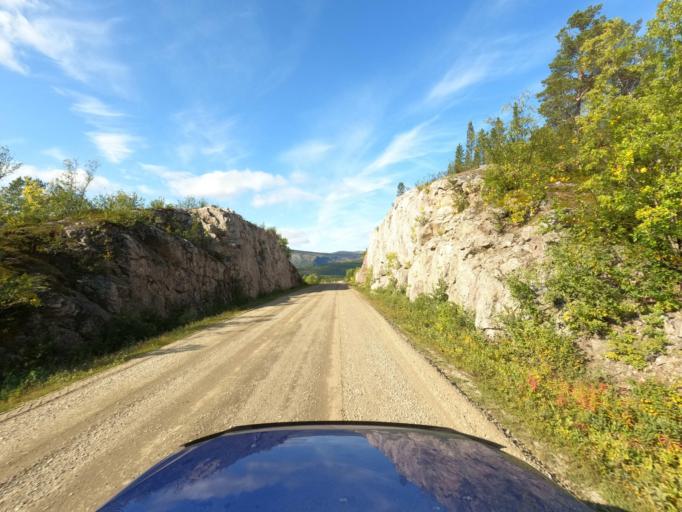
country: NO
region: Finnmark Fylke
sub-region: Porsanger
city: Lakselv
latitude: 69.8902
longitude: 25.0030
